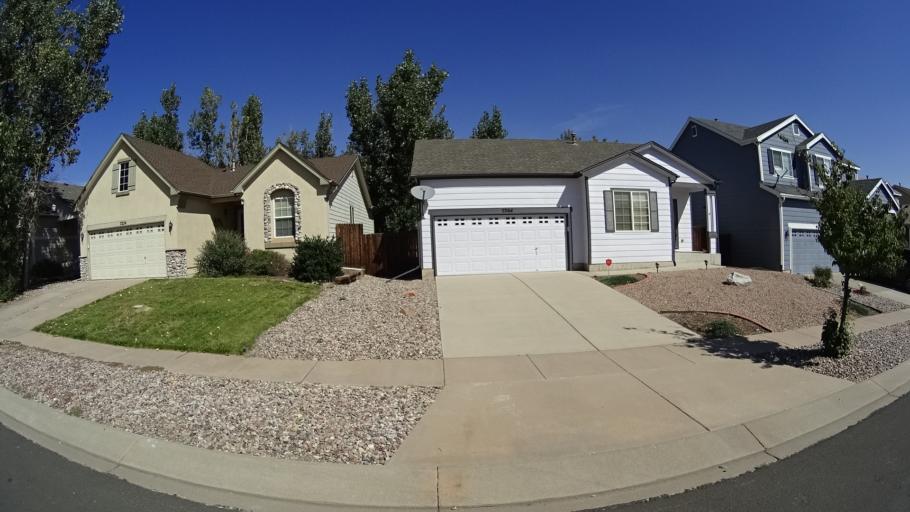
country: US
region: Colorado
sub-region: El Paso County
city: Cimarron Hills
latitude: 38.8958
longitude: -104.6933
